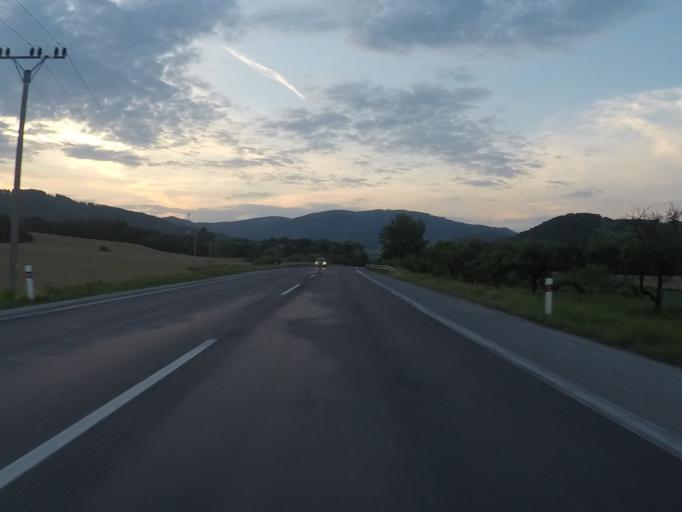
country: SK
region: Banskobystricky
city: Rimavska Sobota
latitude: 48.4884
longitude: 19.9429
